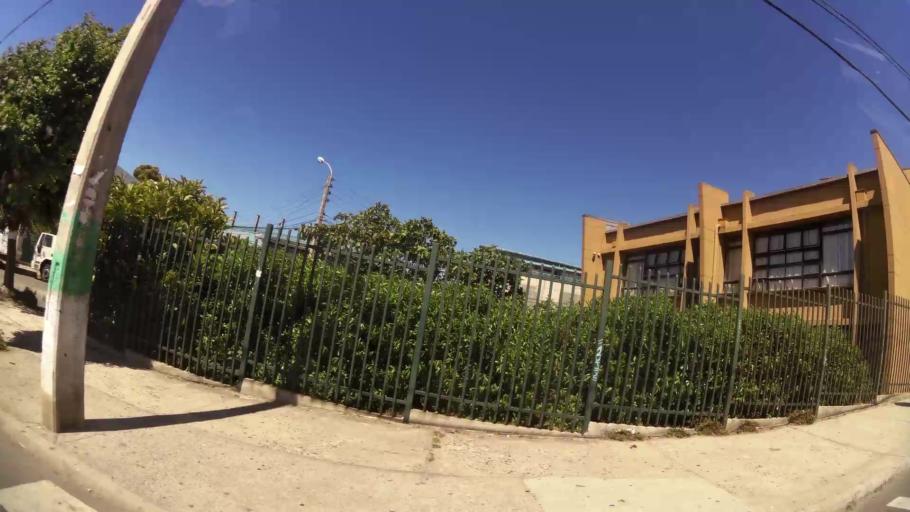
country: CL
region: Valparaiso
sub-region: Provincia de Valparaiso
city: Valparaiso
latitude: -33.0261
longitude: -71.6395
